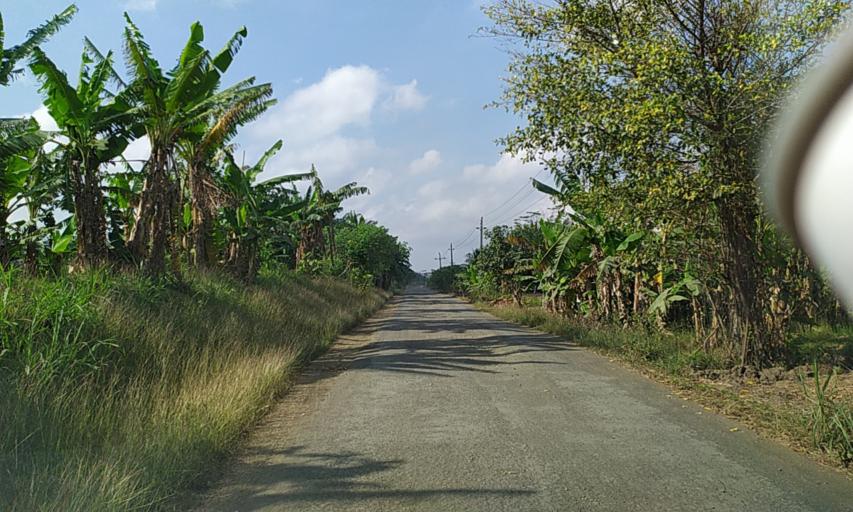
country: ID
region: Central Java
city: Sidakaya
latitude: -7.5988
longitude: 108.8715
